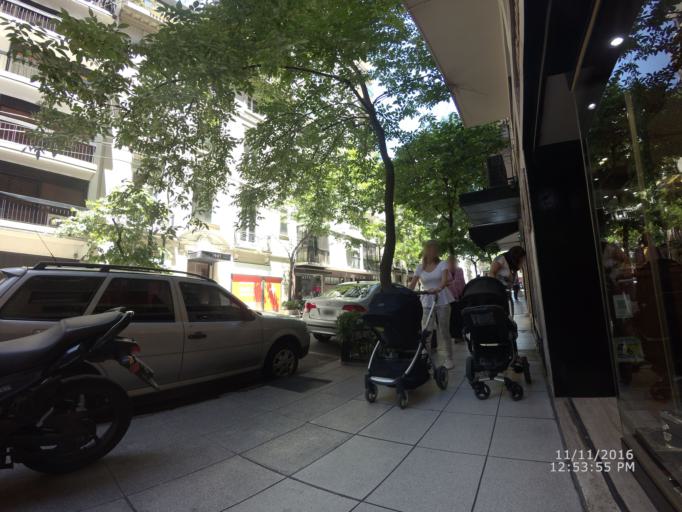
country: AR
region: Buenos Aires F.D.
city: Retiro
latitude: -34.5877
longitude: -58.3894
